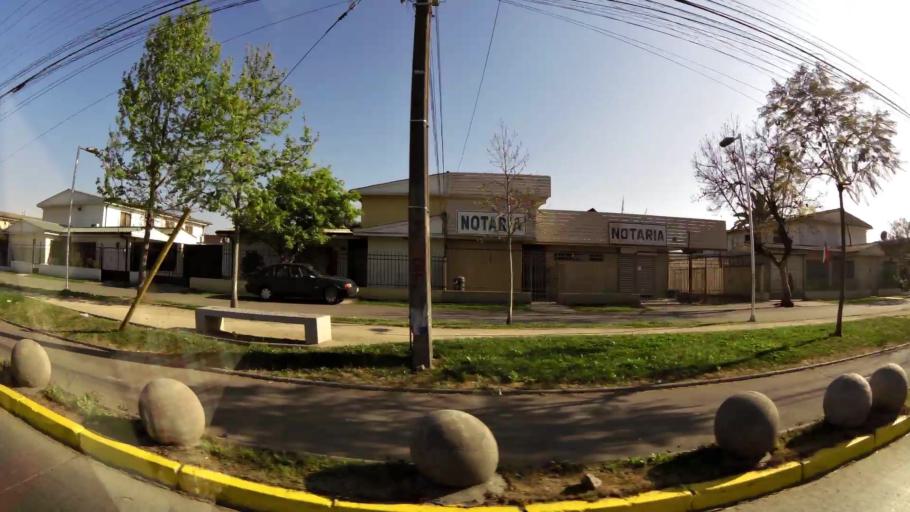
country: CL
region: Santiago Metropolitan
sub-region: Provincia de Santiago
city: Santiago
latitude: -33.3972
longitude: -70.6678
